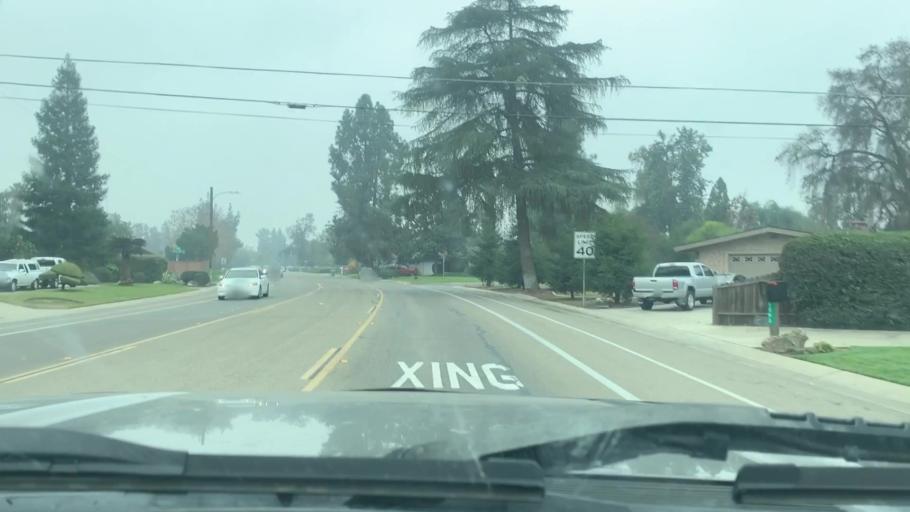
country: US
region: California
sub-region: Tulare County
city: Visalia
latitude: 36.3174
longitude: -119.3265
